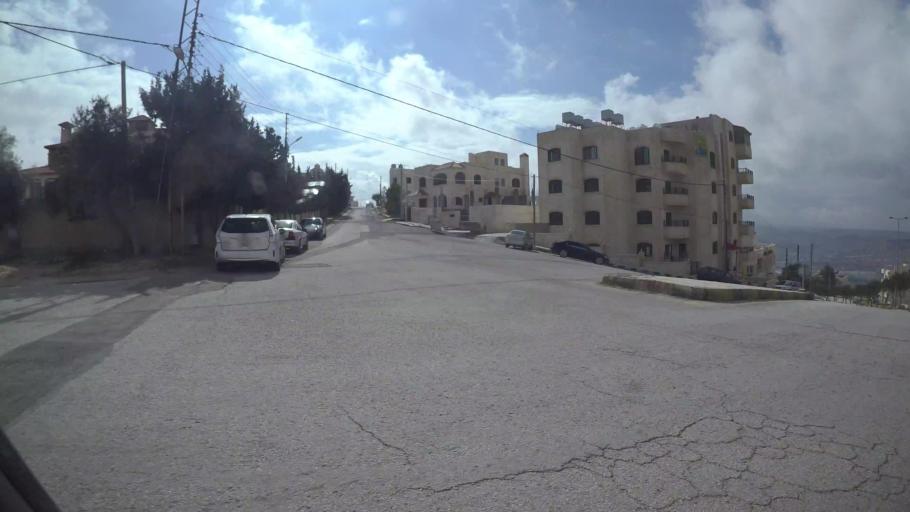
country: JO
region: Amman
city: Al Jubayhah
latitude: 32.0723
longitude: 35.8817
